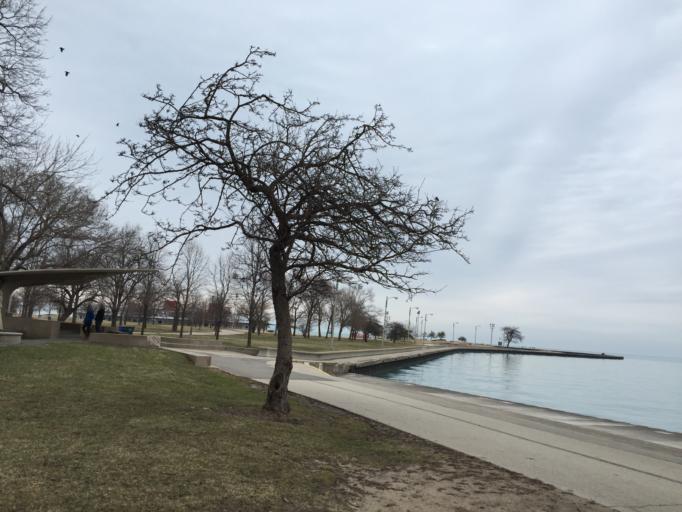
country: US
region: Illinois
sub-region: Cook County
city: Chicago
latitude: 41.9110
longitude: -87.6250
